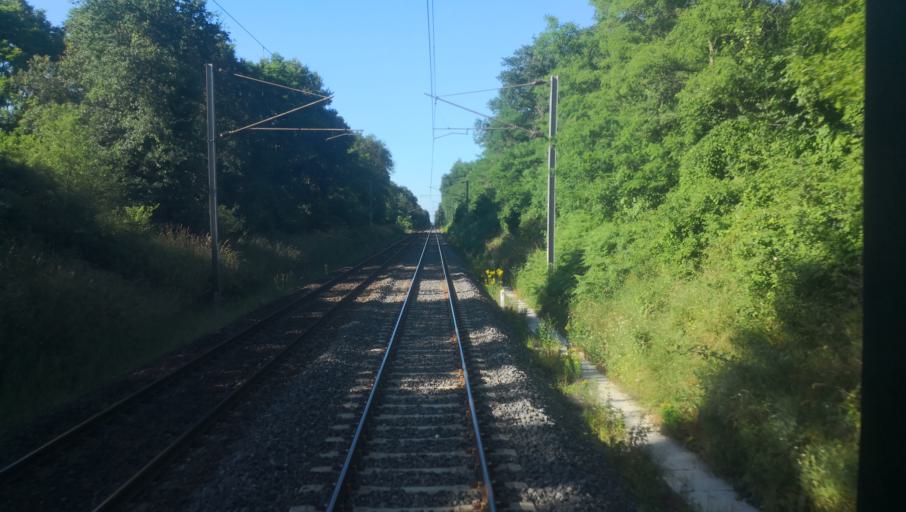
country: FR
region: Centre
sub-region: Departement du Cher
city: Saint-Satur
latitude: 47.3457
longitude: 2.8815
